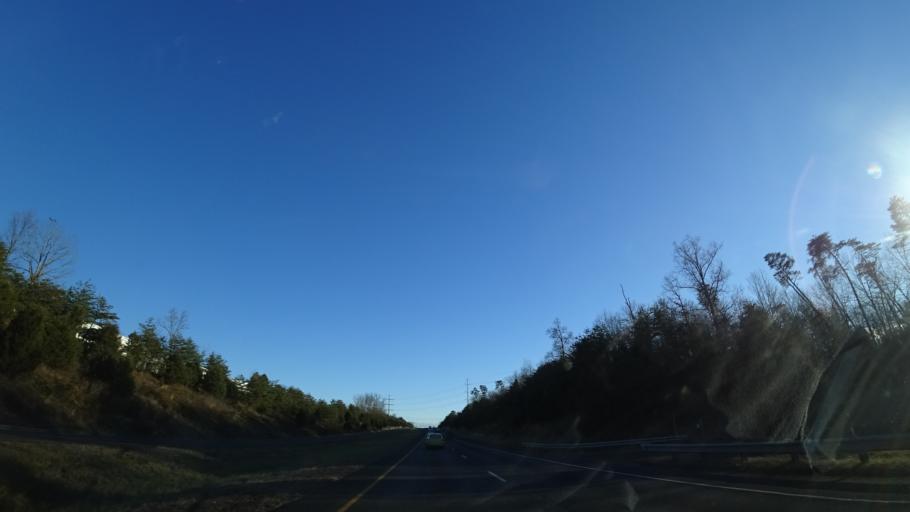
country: US
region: Virginia
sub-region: Prince William County
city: Bull Run
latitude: 38.7806
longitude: -77.5455
